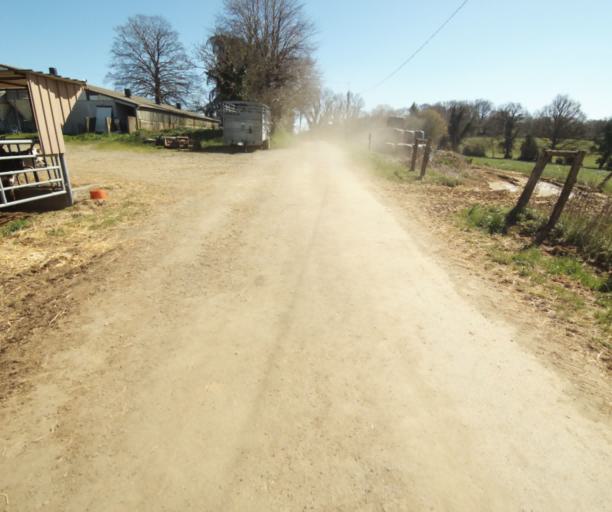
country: FR
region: Limousin
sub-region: Departement de la Correze
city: Uzerche
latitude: 45.4033
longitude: 1.6324
